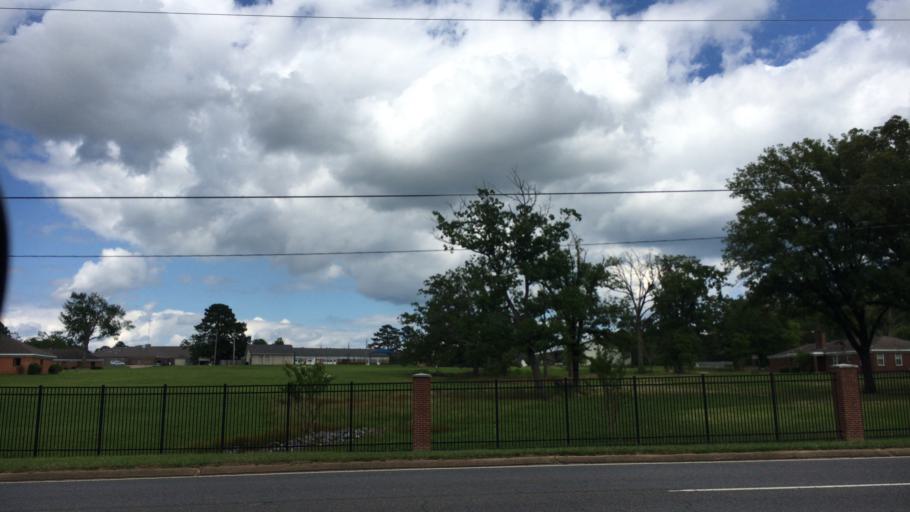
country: US
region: Louisiana
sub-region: Lincoln Parish
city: Ruston
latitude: 32.5159
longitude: -92.6386
